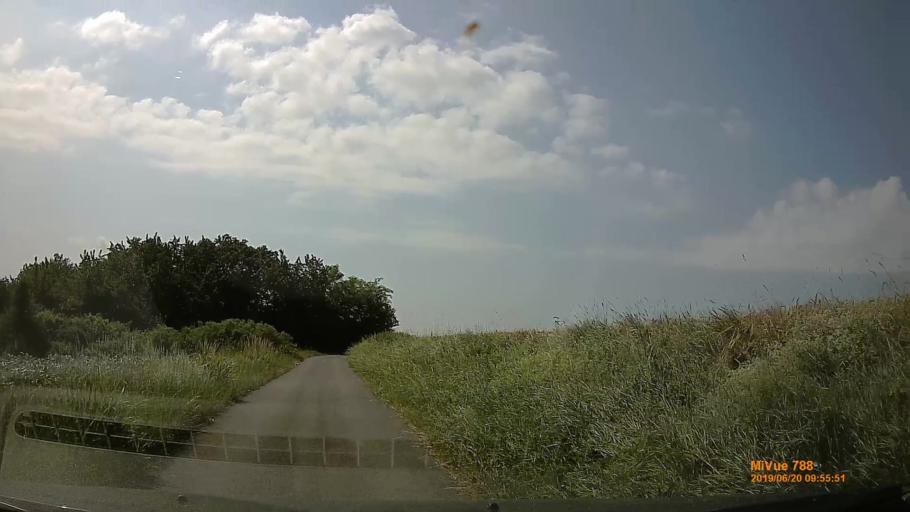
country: HU
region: Baranya
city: Pecsvarad
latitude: 46.1702
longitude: 18.4693
